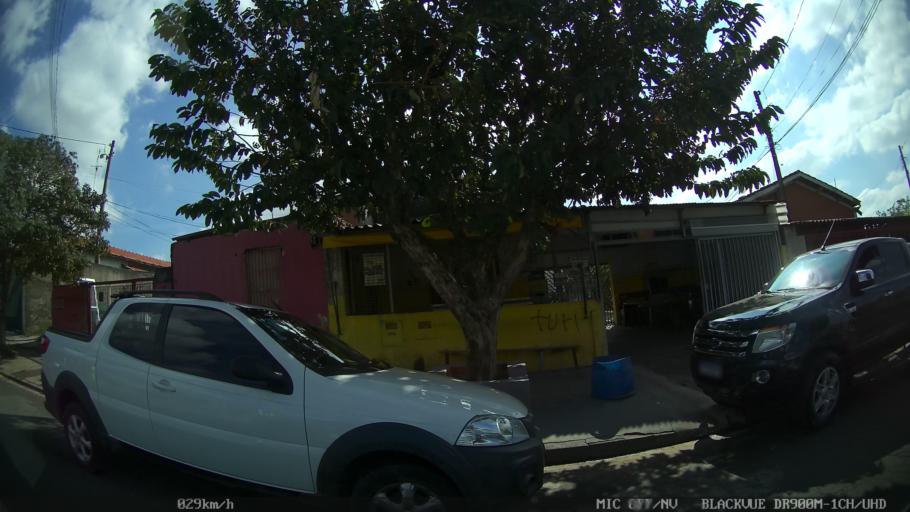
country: BR
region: Sao Paulo
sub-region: Campinas
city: Campinas
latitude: -22.9372
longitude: -47.1123
